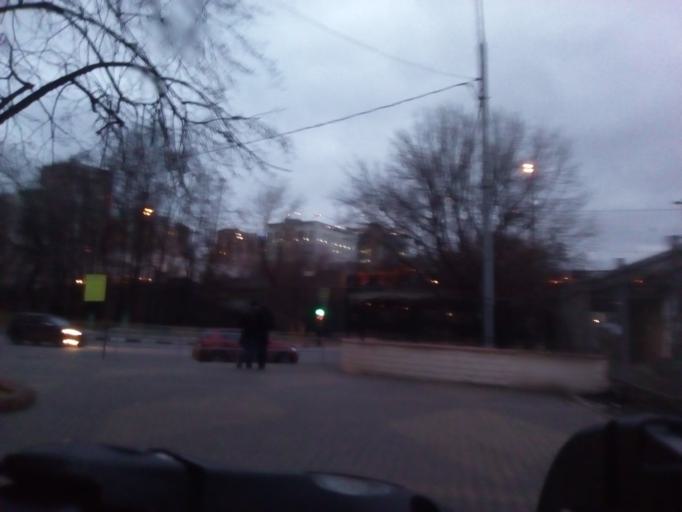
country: RU
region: Moscow
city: Lefortovo
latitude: 55.7511
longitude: 37.7200
